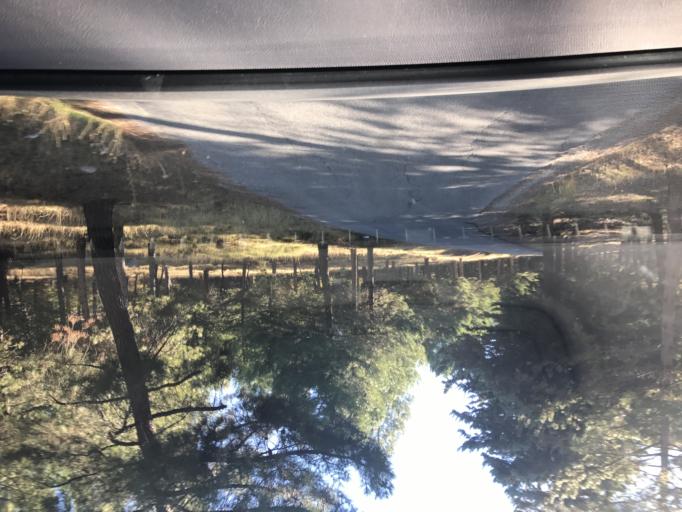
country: ES
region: Andalusia
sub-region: Provincia de Granada
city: Beas de Granada
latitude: 37.3053
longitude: -3.4501
